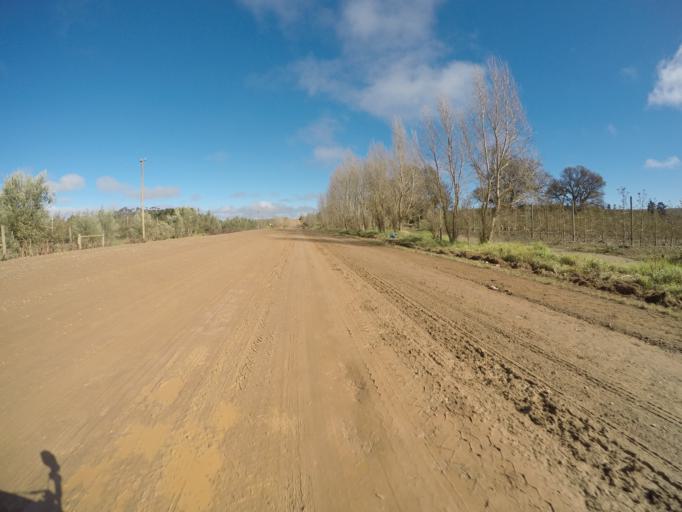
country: ZA
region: Western Cape
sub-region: Overberg District Municipality
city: Caledon
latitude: -34.1117
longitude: 19.7467
